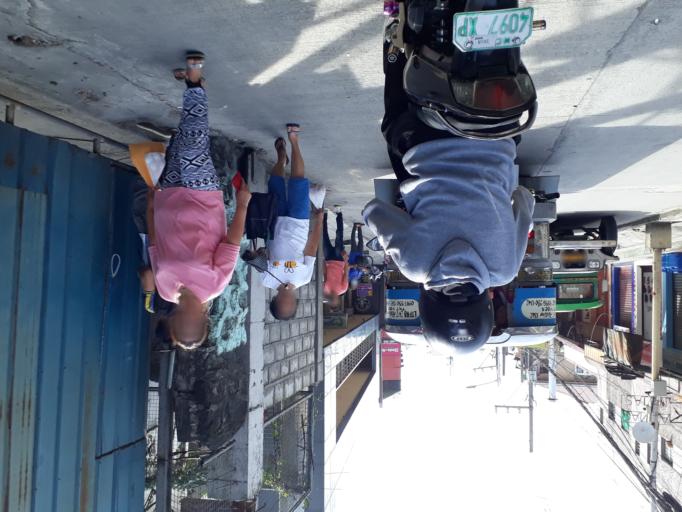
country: PH
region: Calabarzon
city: Bagong Pagasa
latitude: 14.6778
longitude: 121.0060
